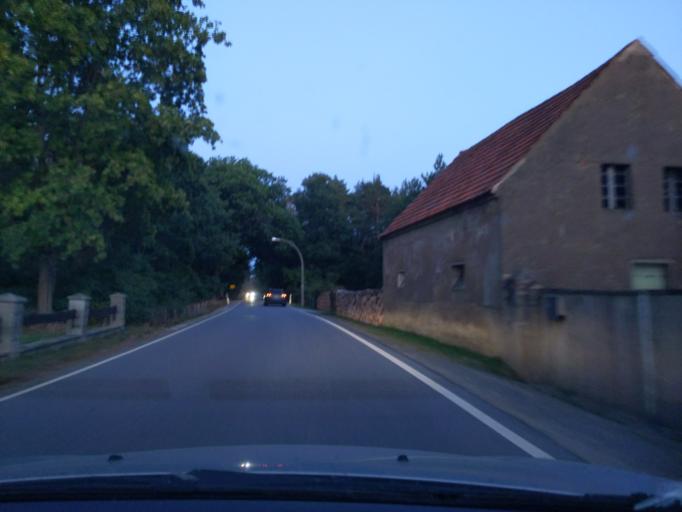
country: DE
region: Saxony
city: Lohsa
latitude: 51.3305
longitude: 14.3908
